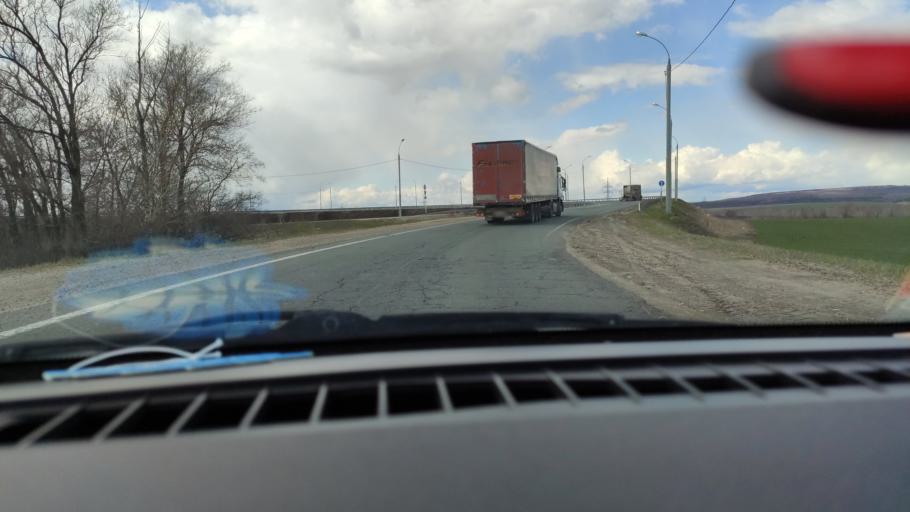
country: RU
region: Samara
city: Varlamovo
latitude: 53.1974
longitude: 48.2919
